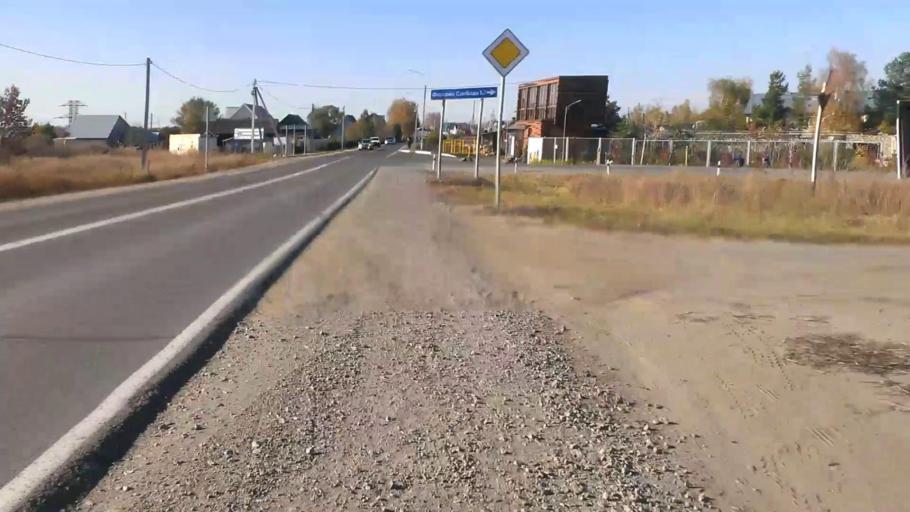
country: RU
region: Altai Krai
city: Sannikovo
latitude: 53.3133
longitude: 83.9629
